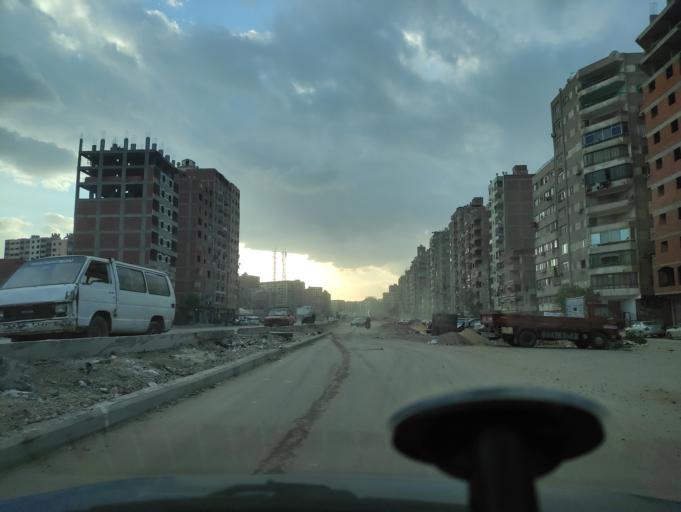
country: EG
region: Muhafazat al Qalyubiyah
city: Al Khankah
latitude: 30.1346
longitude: 31.3284
